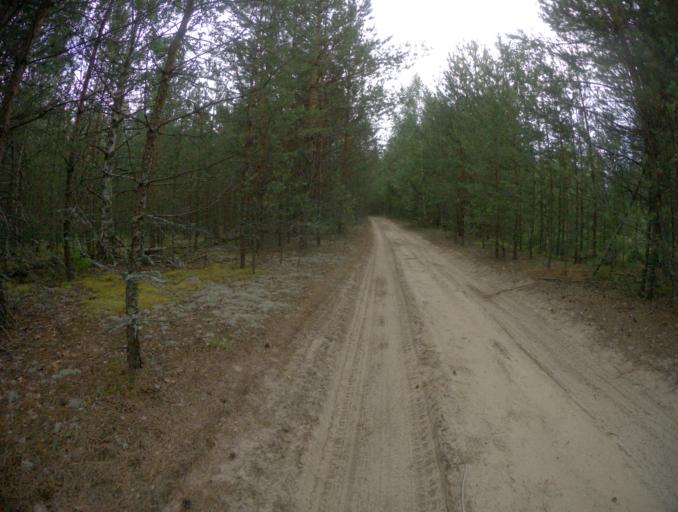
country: RU
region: Nizjnij Novgorod
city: Frolishchi
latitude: 56.4677
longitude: 42.6762
